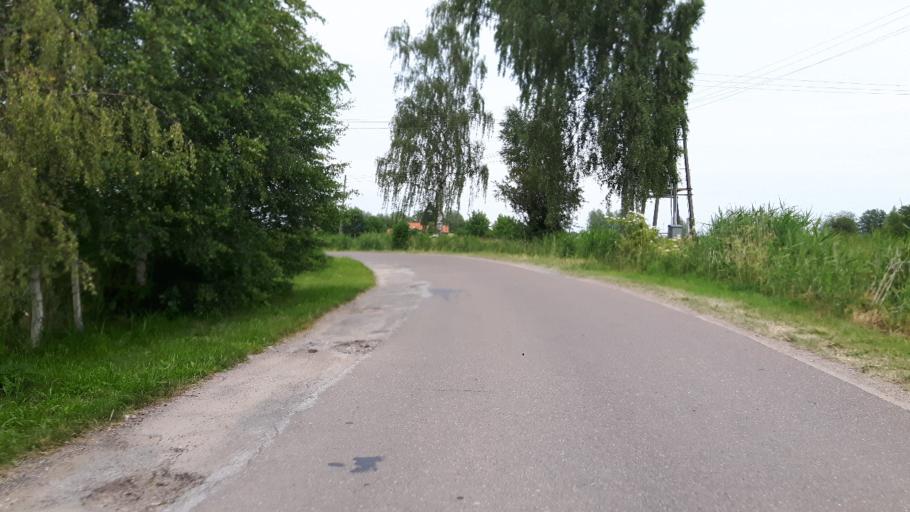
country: PL
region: Pomeranian Voivodeship
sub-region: Powiat nowodworski
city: Sztutowo
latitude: 54.2637
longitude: 19.1662
